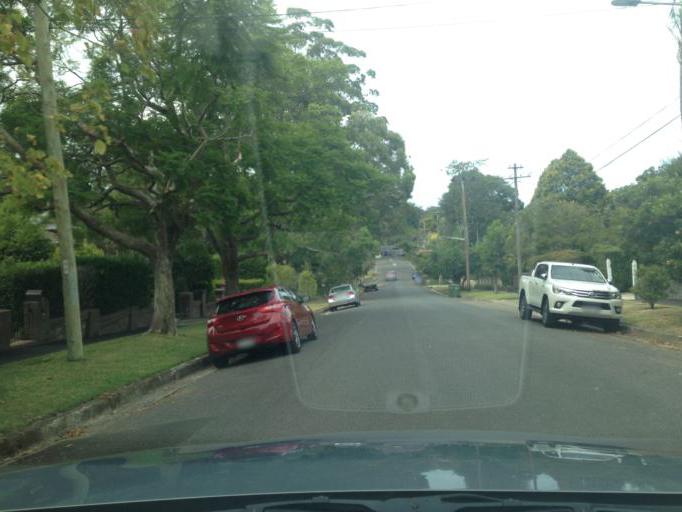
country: AU
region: New South Wales
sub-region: Ku-ring-gai
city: Killara
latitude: -33.7676
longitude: 151.1666
